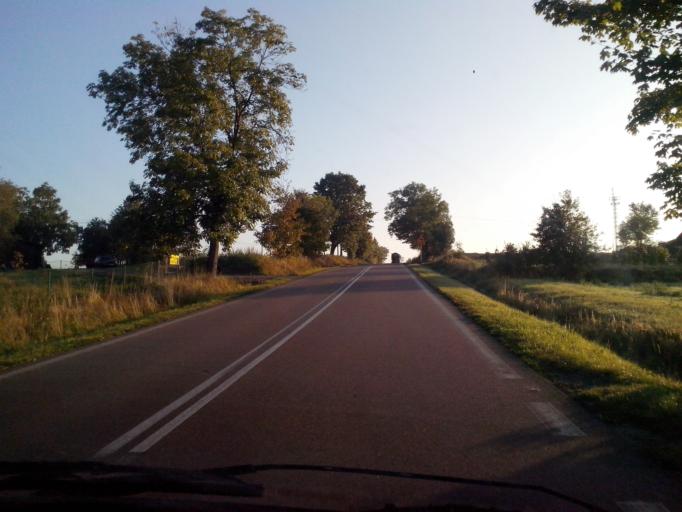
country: PL
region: Subcarpathian Voivodeship
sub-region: Powiat brzozowski
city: Wesola
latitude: 49.8274
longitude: 22.0837
